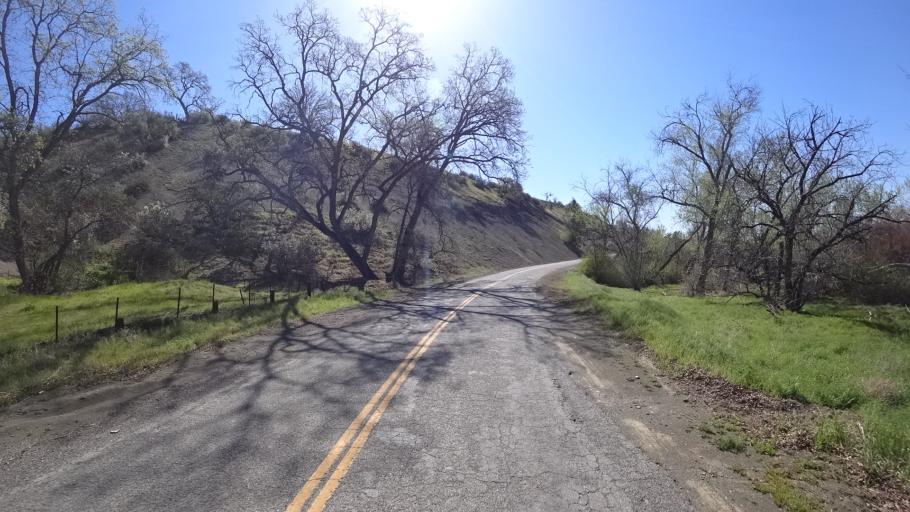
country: US
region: California
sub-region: Glenn County
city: Orland
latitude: 39.6787
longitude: -122.5246
